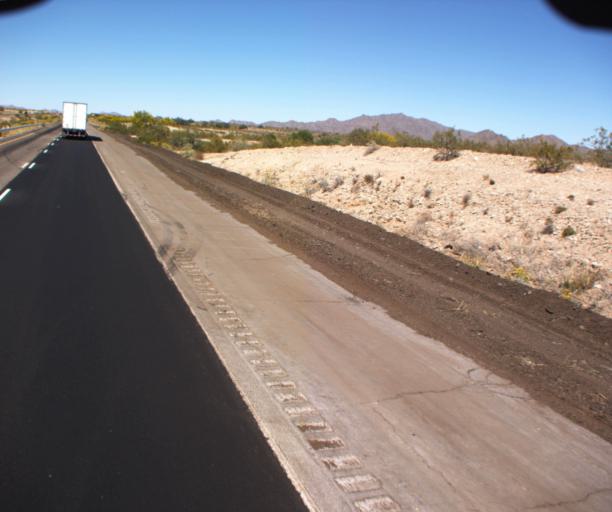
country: US
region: Arizona
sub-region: Maricopa County
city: Gila Bend
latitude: 33.0795
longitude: -112.6468
